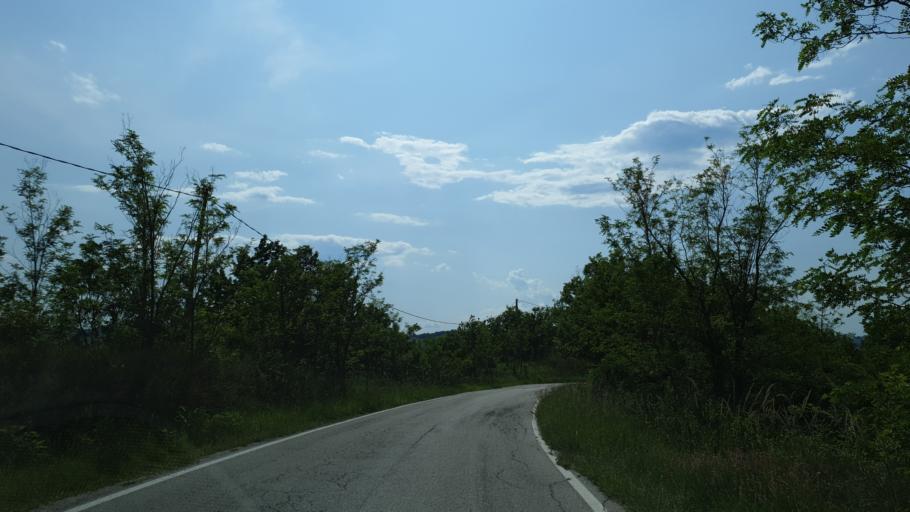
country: IT
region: Emilia-Romagna
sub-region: Provincia di Rimini
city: Sant'Agata Feltria
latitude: 43.9118
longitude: 12.2066
